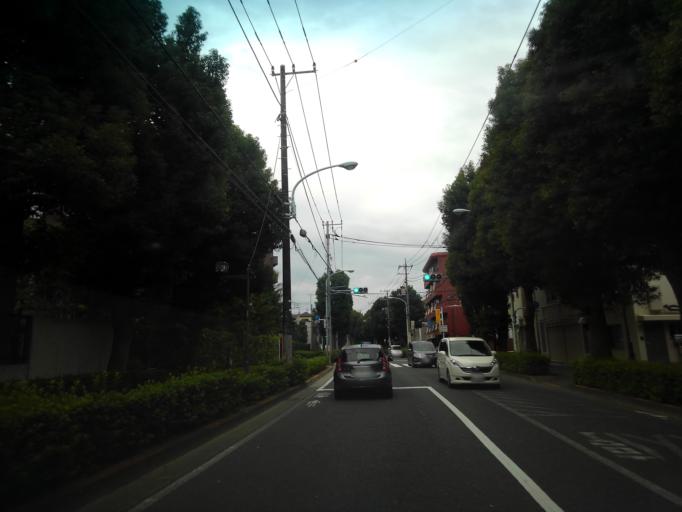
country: JP
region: Tokyo
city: Chofugaoka
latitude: 35.6616
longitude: 139.5414
